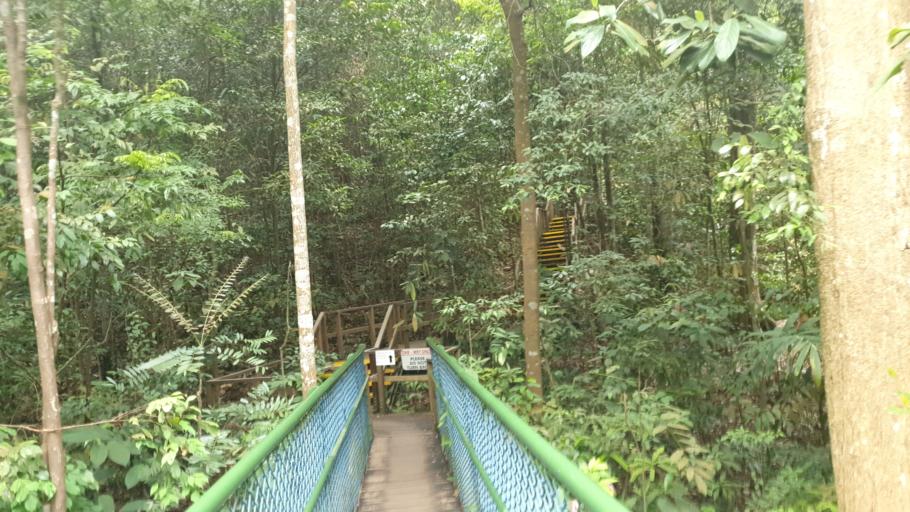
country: SG
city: Singapore
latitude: 1.3613
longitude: 103.8107
